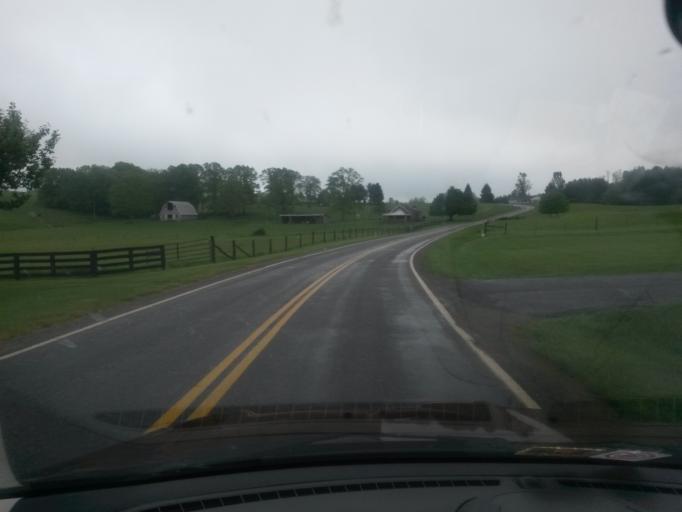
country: US
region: Virginia
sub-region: Patrick County
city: Stuart
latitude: 36.7525
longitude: -80.3920
